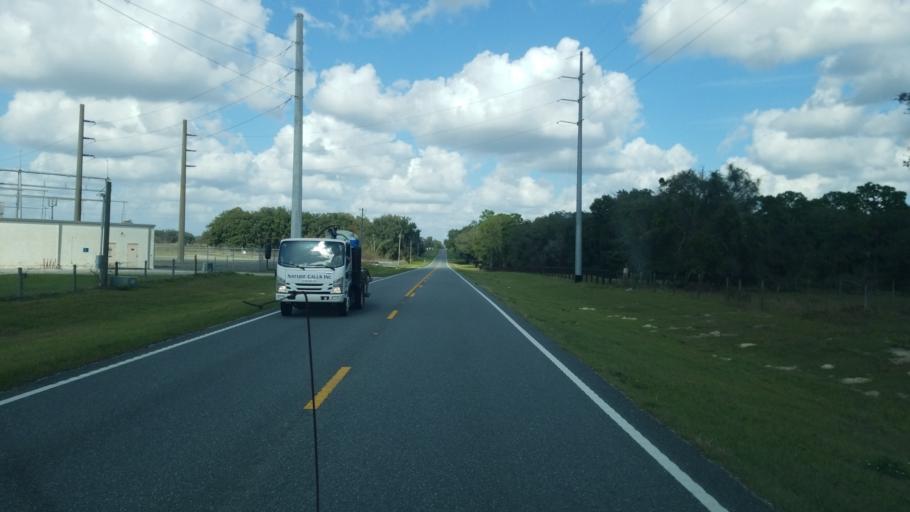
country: US
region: Florida
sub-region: Sumter County
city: Wildwood
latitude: 28.8976
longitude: -82.1200
